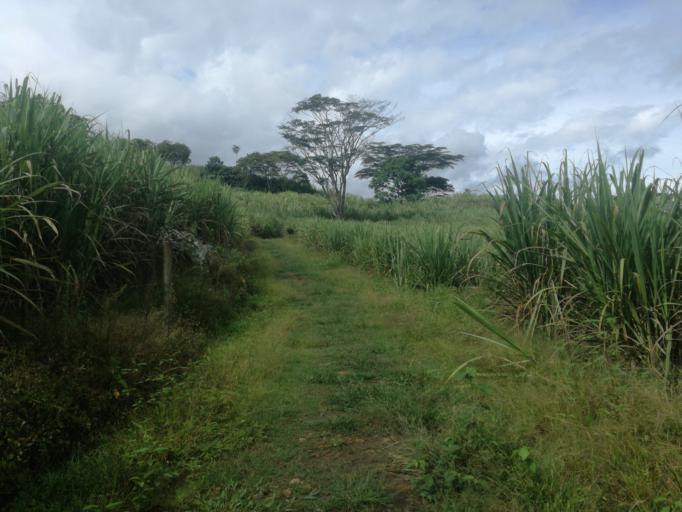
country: CO
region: Boyaca
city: Santana
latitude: 6.0598
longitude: -73.4859
